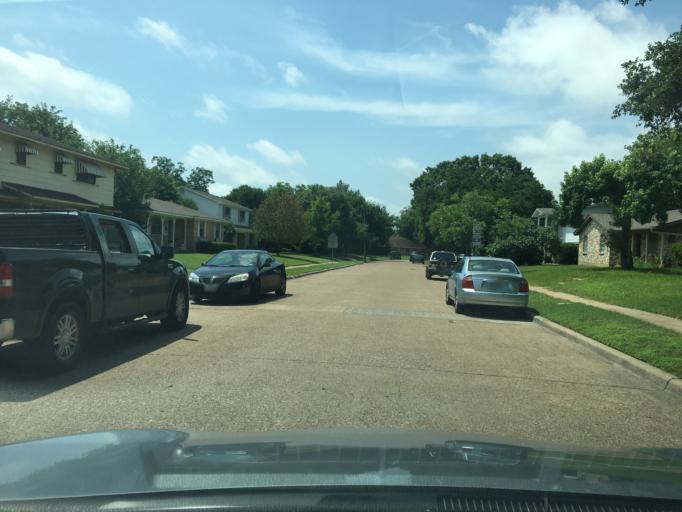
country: US
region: Texas
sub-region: Dallas County
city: Garland
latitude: 32.9233
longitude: -96.6793
